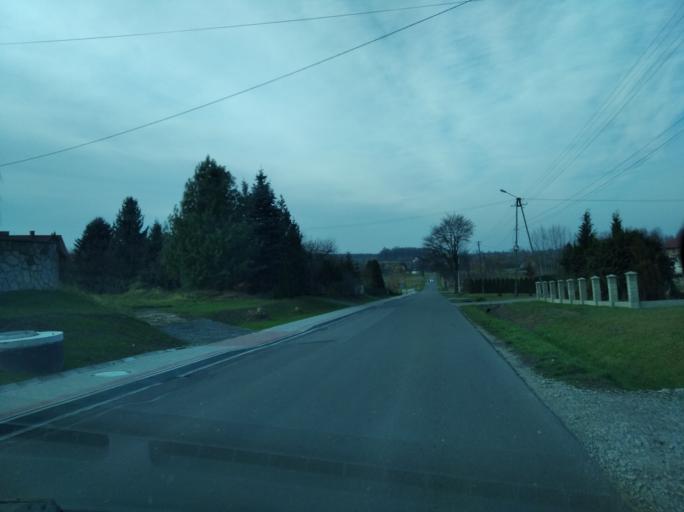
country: PL
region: Subcarpathian Voivodeship
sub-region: Powiat ropczycko-sedziszowski
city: Iwierzyce
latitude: 50.0323
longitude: 21.7516
